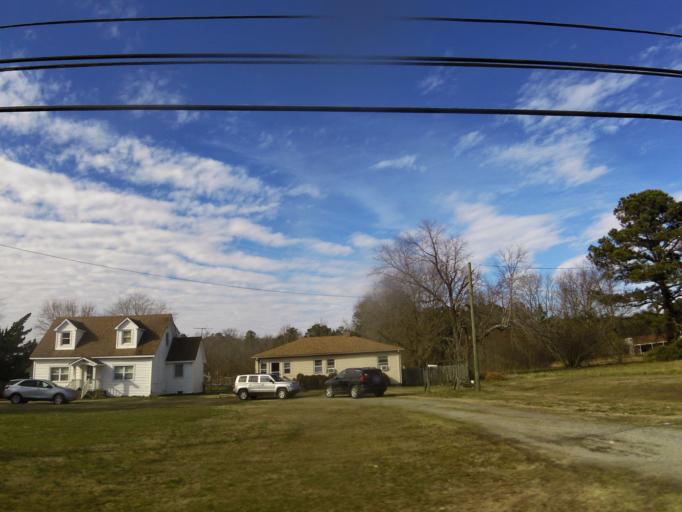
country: US
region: Virginia
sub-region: City of Franklin
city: Franklin
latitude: 36.6865
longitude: -76.9071
